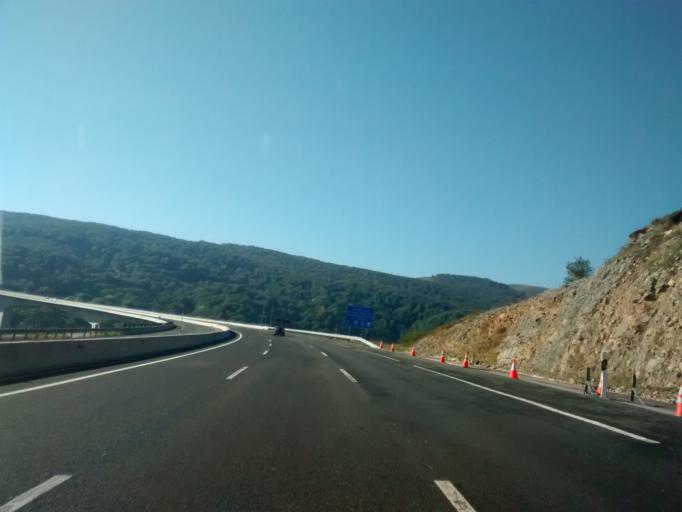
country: ES
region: Cantabria
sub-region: Provincia de Cantabria
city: Pesquera
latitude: 43.1082
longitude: -4.0901
